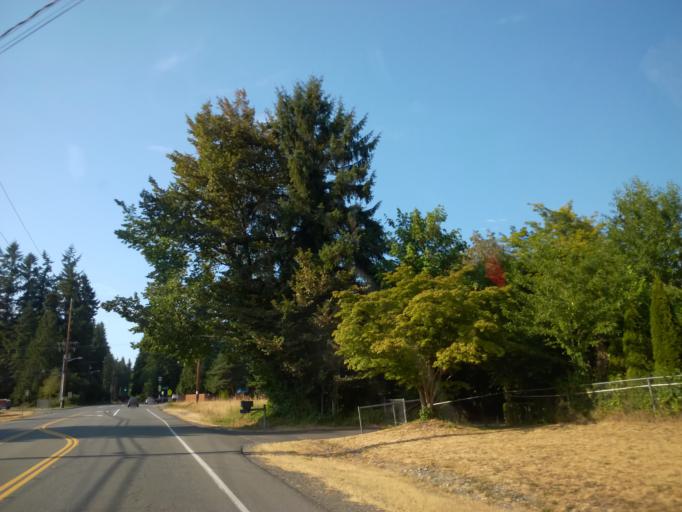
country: US
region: Washington
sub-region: King County
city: Cottage Lake
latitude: 47.7433
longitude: -122.0810
